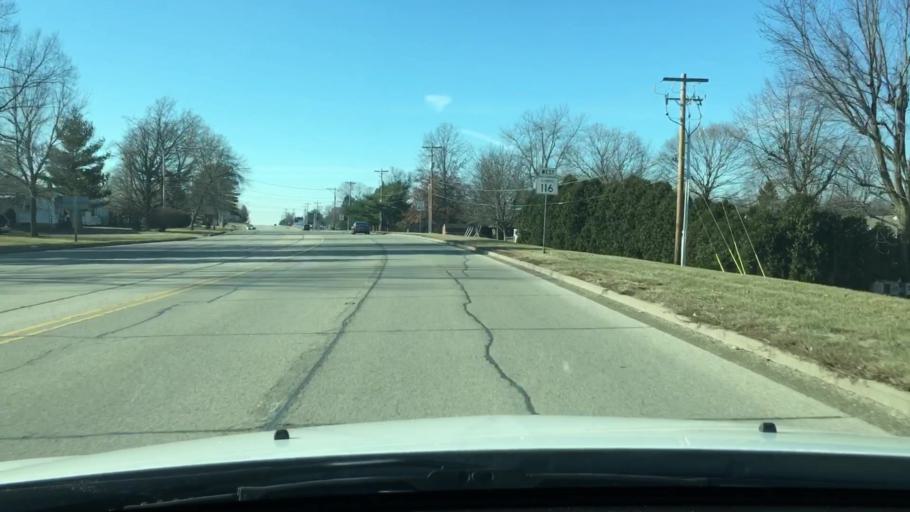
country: US
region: Illinois
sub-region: Woodford County
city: Metamora
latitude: 40.7901
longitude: -89.3766
